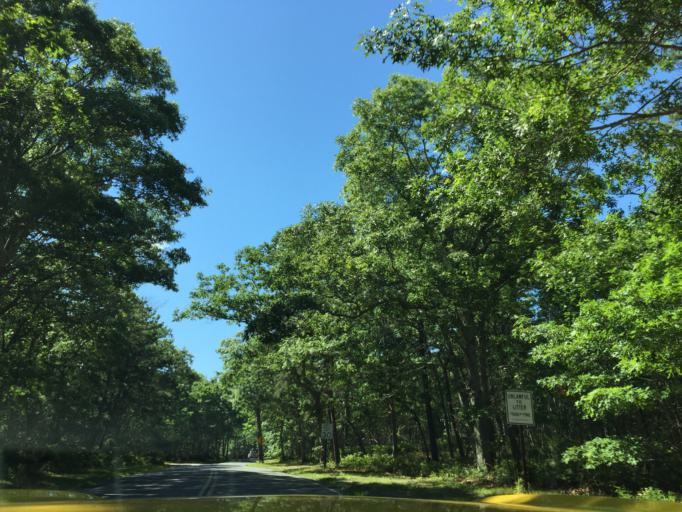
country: US
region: New York
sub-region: Suffolk County
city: East Hampton North
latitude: 40.9533
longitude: -72.2341
